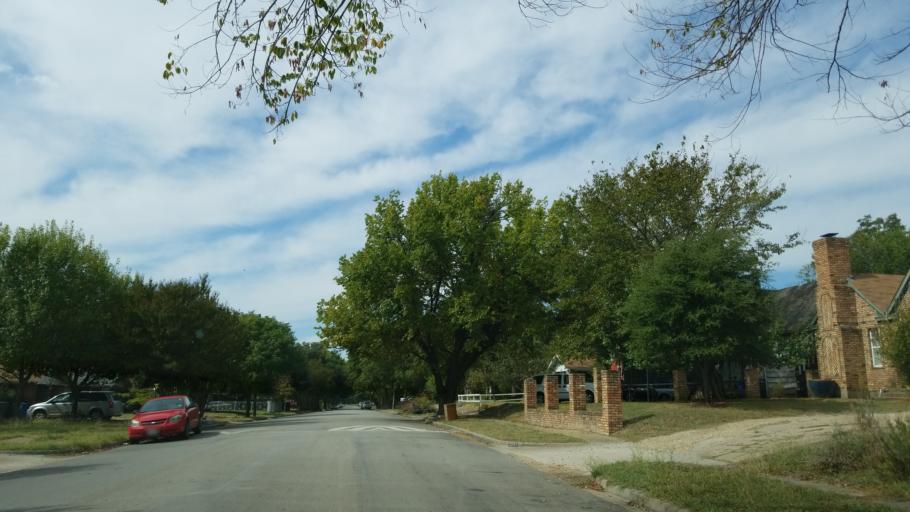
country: US
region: Texas
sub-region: Dallas County
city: Dallas
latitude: 32.7894
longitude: -96.7382
